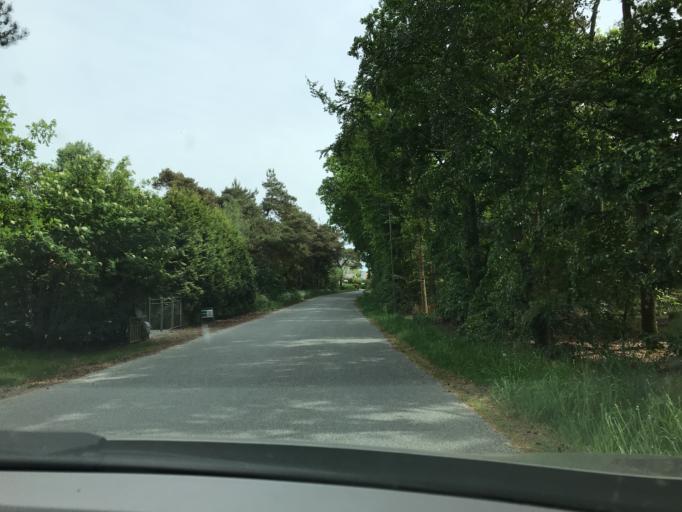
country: DK
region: Central Jutland
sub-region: Norddjurs Kommune
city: Allingabro
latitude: 56.6035
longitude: 10.3061
